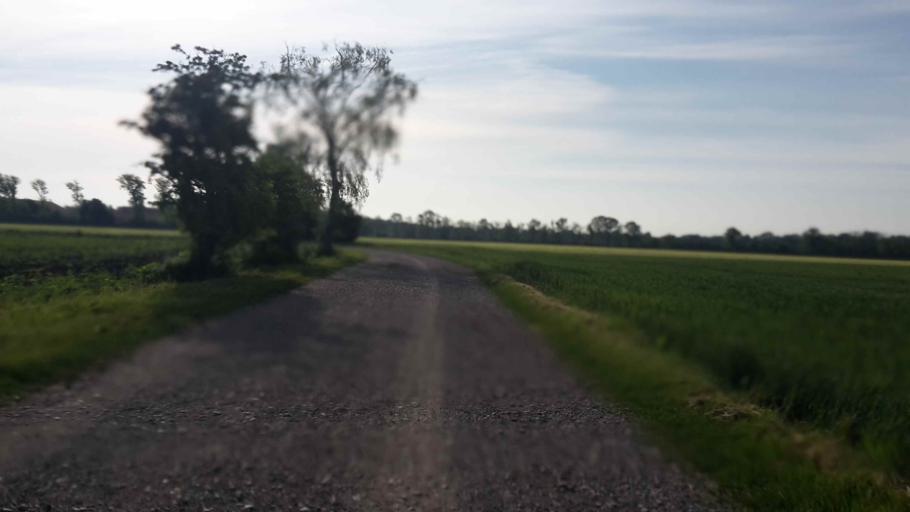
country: DE
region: Bavaria
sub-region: Upper Bavaria
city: Oberschleissheim
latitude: 48.2459
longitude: 11.5382
